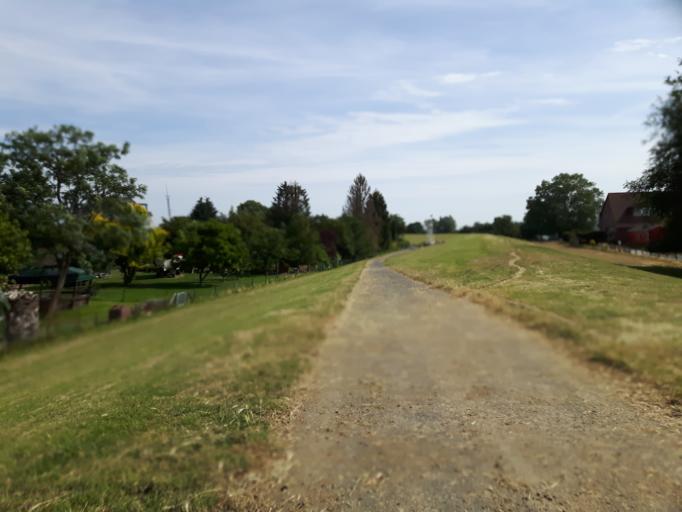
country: DE
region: Lower Saxony
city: Elsfleth
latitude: 53.2522
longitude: 8.4706
